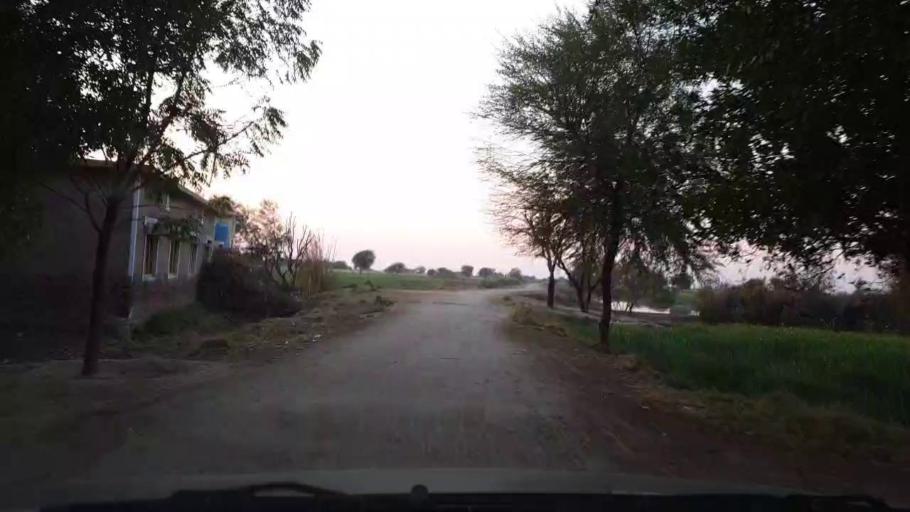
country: PK
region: Sindh
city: Jhol
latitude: 25.9380
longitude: 68.9578
